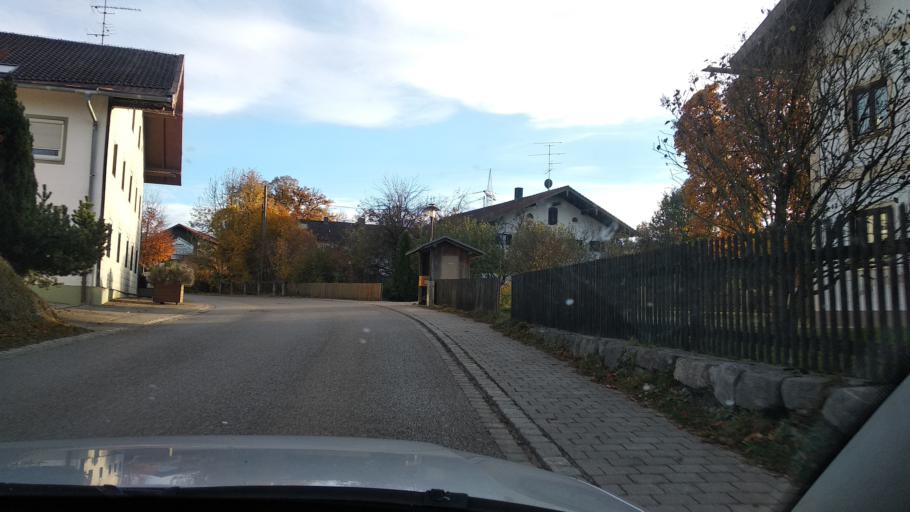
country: DE
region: Bavaria
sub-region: Upper Bavaria
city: Zorneding
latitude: 48.0597
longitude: 11.8505
